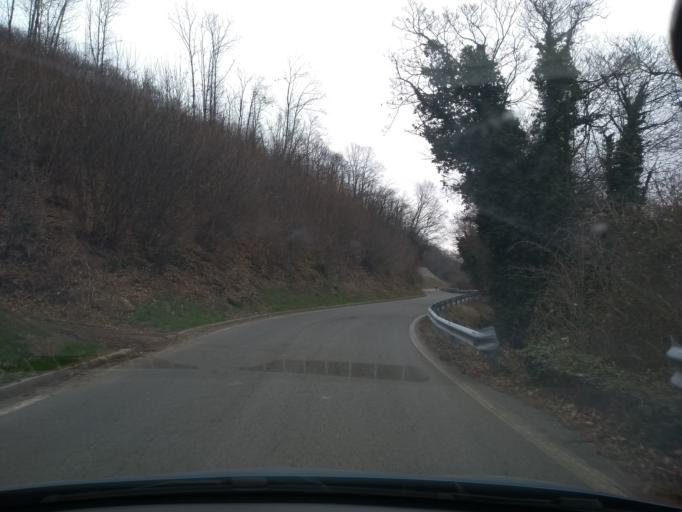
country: IT
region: Piedmont
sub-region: Provincia di Torino
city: Palazzo Canavese
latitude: 45.4704
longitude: 7.9679
